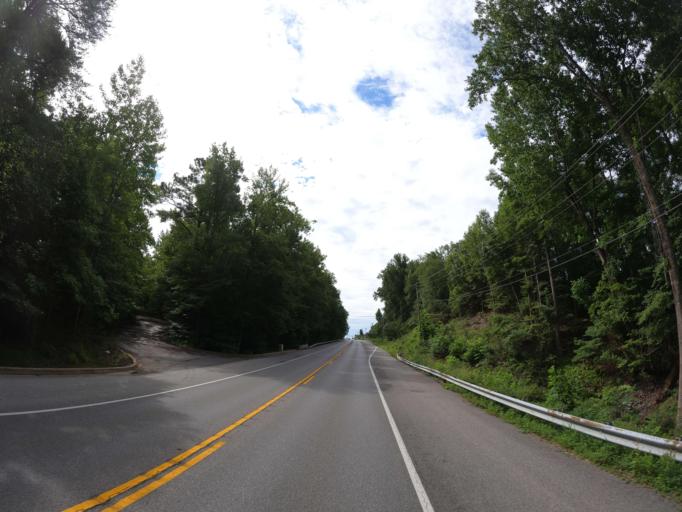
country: US
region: Maryland
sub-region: Saint Mary's County
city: Leonardtown
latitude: 38.2800
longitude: -76.6140
